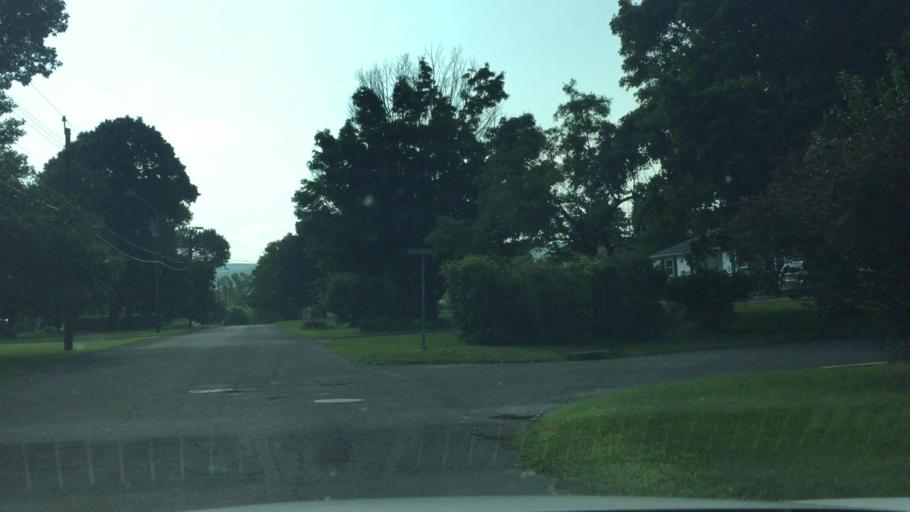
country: US
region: Massachusetts
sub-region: Berkshire County
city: Pittsfield
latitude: 42.4297
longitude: -73.2112
